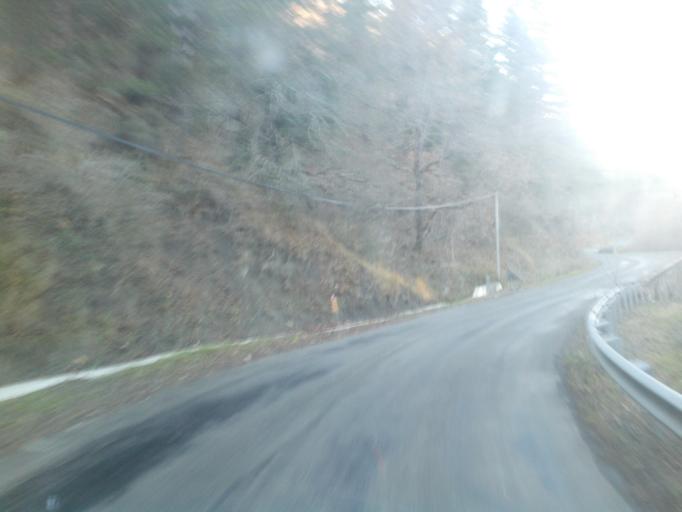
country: FR
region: Languedoc-Roussillon
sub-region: Departement de l'Aude
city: Couiza
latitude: 42.8985
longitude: 2.3129
